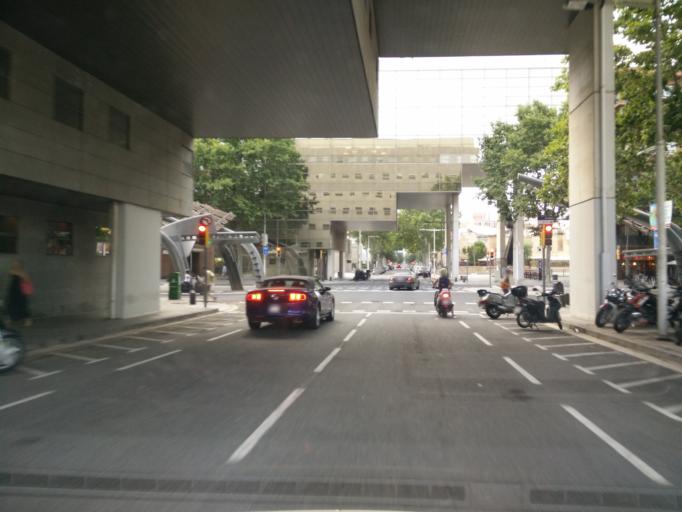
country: ES
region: Catalonia
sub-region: Provincia de Barcelona
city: Ciutat Vella
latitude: 41.3907
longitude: 2.1970
